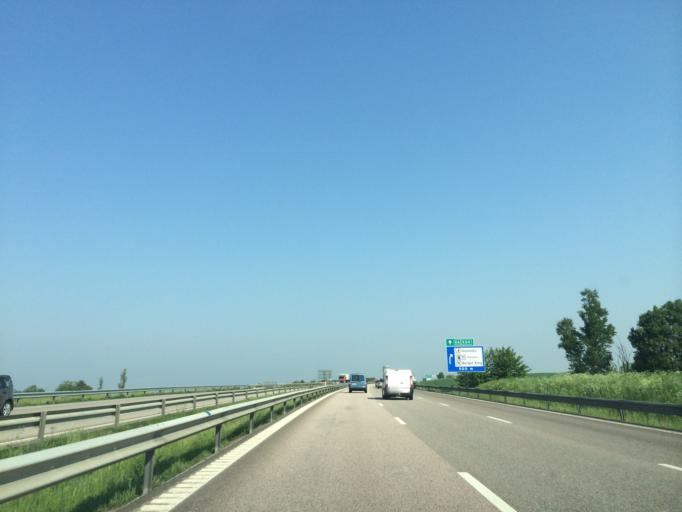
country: SE
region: Skane
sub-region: Helsingborg
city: Glumslov
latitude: 55.9327
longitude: 12.8239
